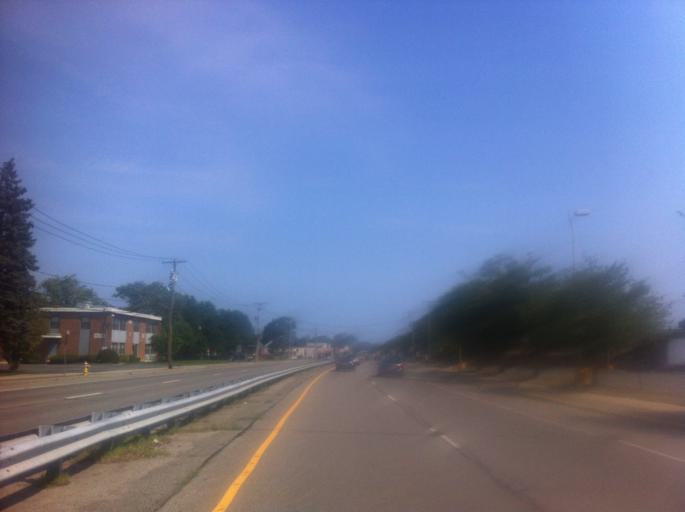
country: US
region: New York
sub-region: Suffolk County
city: West Babylon
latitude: 40.7051
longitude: -73.3462
